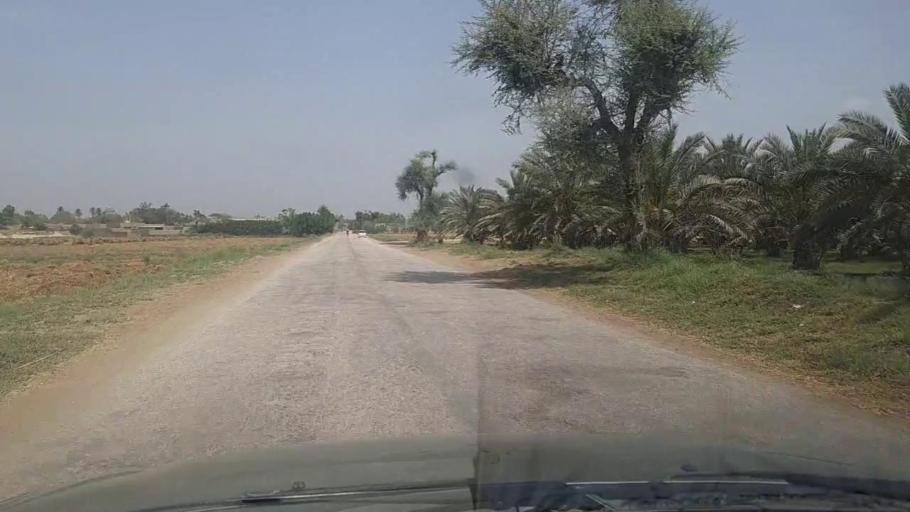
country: PK
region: Sindh
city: Setharja Old
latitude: 27.1637
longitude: 68.5175
